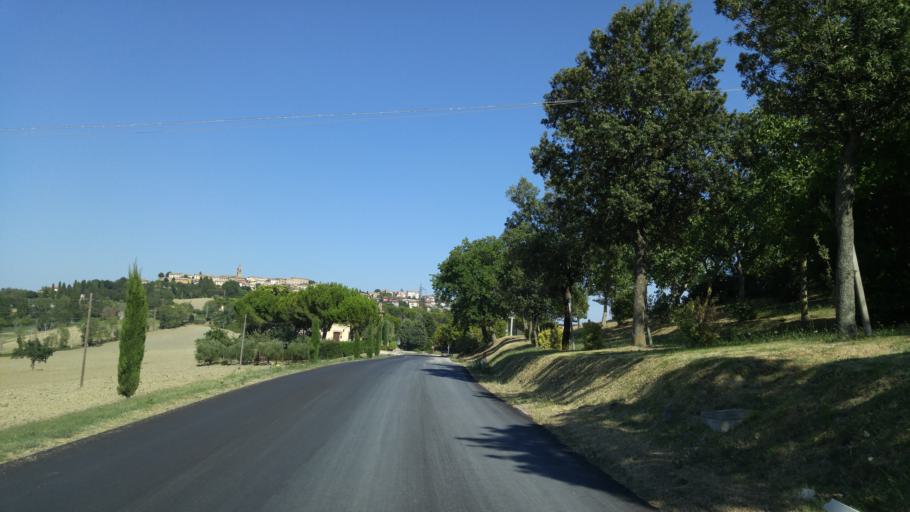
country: IT
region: The Marches
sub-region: Provincia di Pesaro e Urbino
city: Barchi
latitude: 43.6711
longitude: 12.9157
